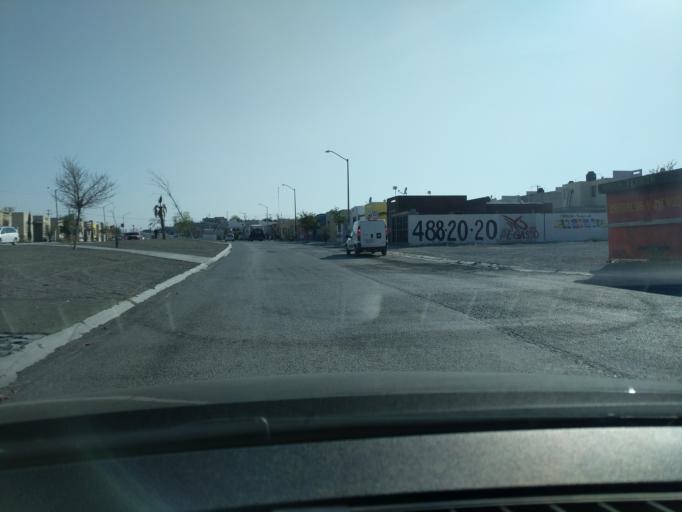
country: MX
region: Coahuila
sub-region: Ramos Arizpe
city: Ramos Arizpe
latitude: 25.5516
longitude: -100.9658
